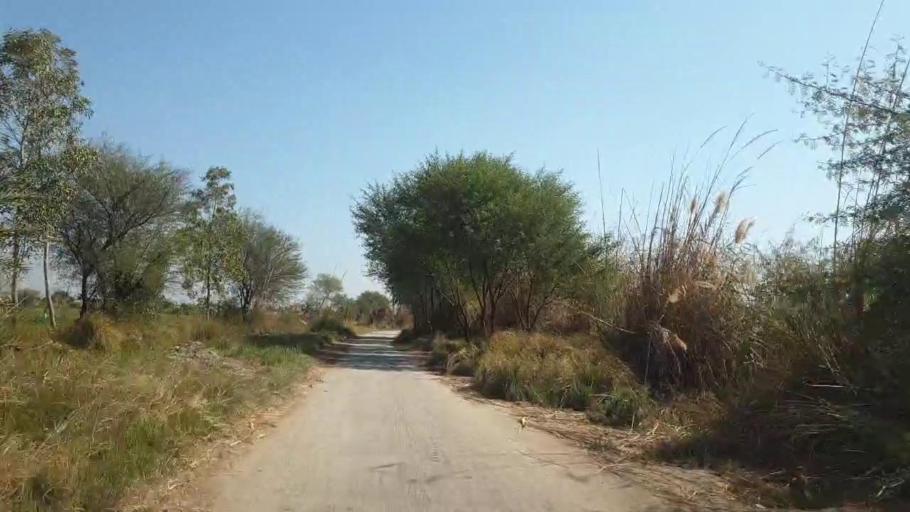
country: PK
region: Sindh
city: Mirpur Khas
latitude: 25.6431
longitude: 69.0273
